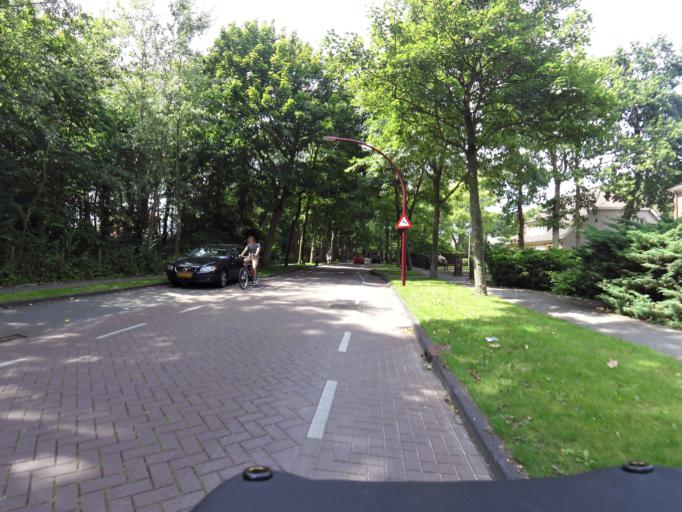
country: NL
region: South Holland
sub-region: Gemeente Brielle
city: Brielle
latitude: 51.9144
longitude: 4.0932
